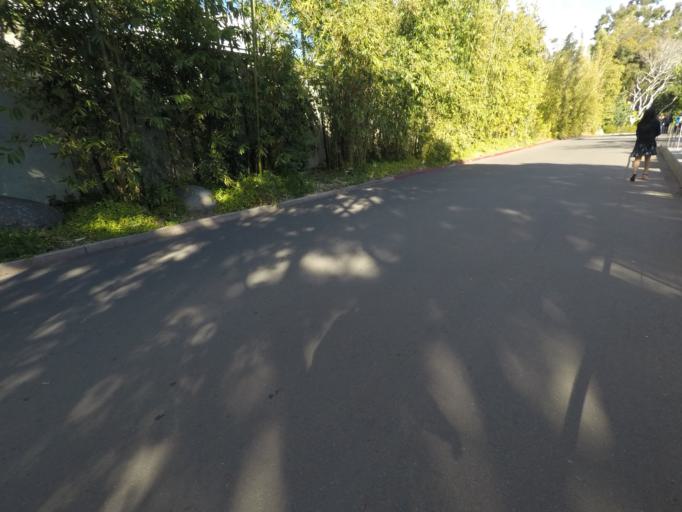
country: US
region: California
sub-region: San Diego County
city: San Diego
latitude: 32.7393
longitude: -117.1507
